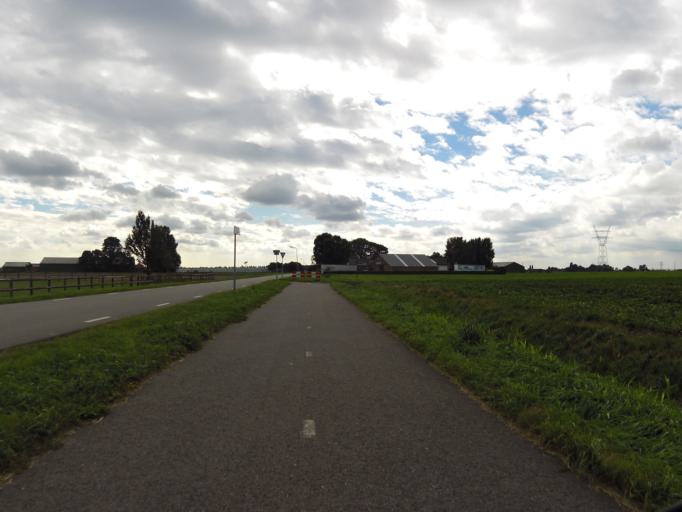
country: NL
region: South Holland
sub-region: Gemeente Rijnwoude
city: Benthuizen
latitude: 52.0593
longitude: 4.5758
